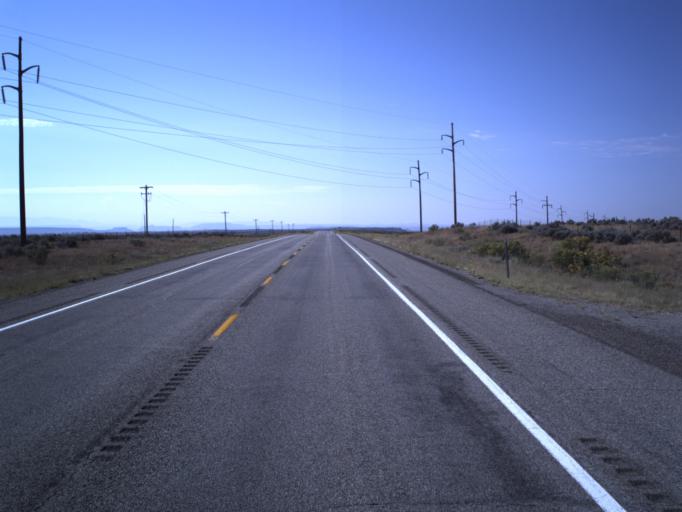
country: US
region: Utah
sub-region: San Juan County
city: Blanding
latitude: 37.5231
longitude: -109.4941
